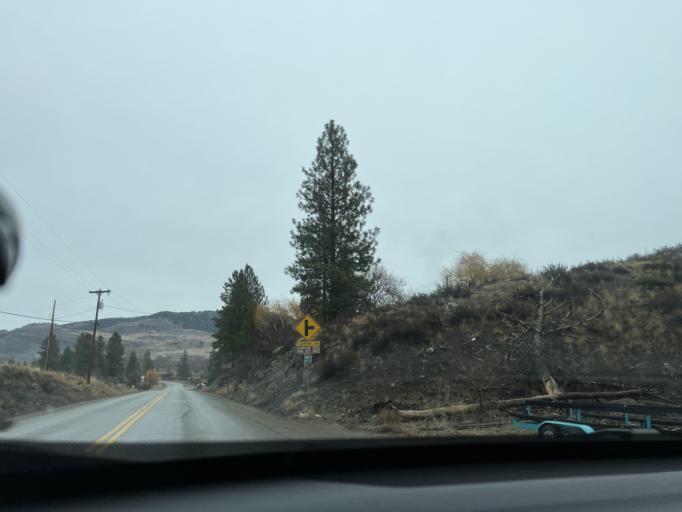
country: US
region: Washington
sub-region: Okanogan County
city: Brewster
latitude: 48.4954
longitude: -120.1764
